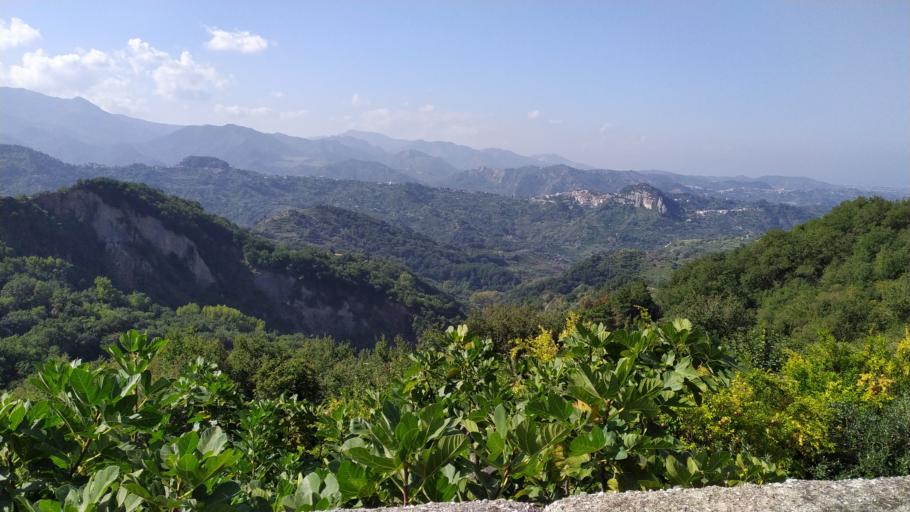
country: IT
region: Sicily
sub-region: Messina
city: Rometta
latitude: 38.1612
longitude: 15.4186
